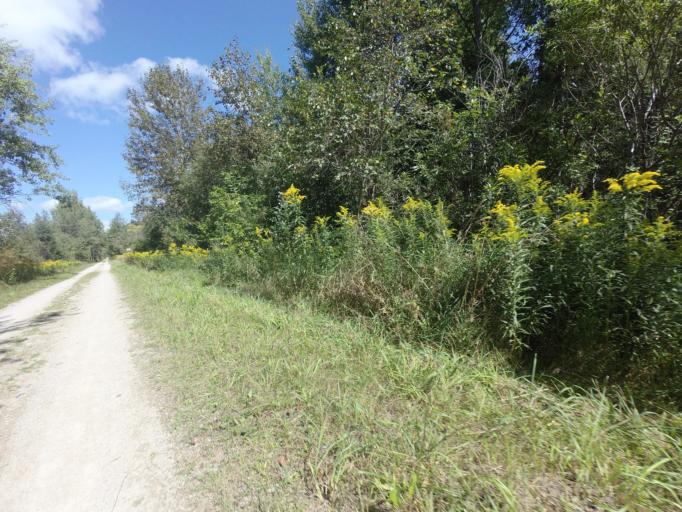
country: CA
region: Ontario
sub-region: Wellington County
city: Guelph
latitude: 43.7548
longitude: -80.3212
